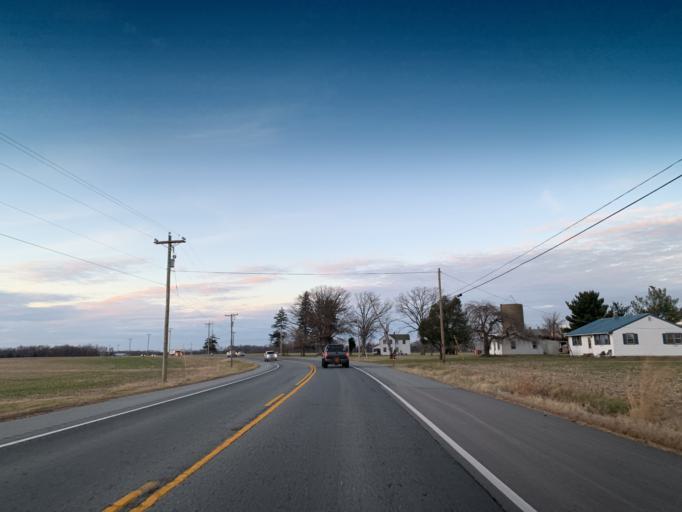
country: US
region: Delaware
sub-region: New Castle County
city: Middletown
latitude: 39.4378
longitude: -75.8619
